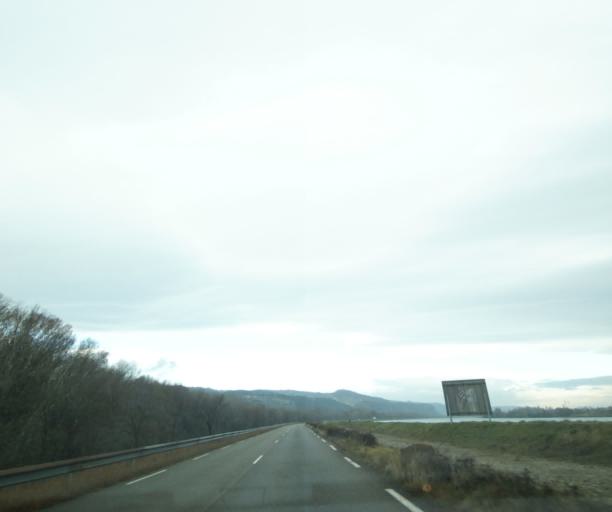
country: FR
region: Rhone-Alpes
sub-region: Departement de l'Ardeche
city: Cornas
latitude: 44.9641
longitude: 4.8656
